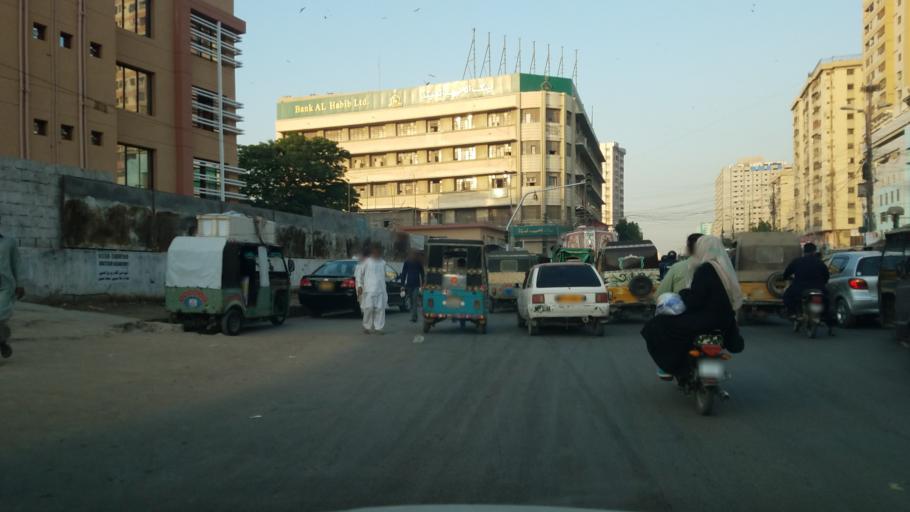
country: PK
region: Sindh
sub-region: Karachi District
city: Karachi
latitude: 24.8649
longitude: 67.0243
